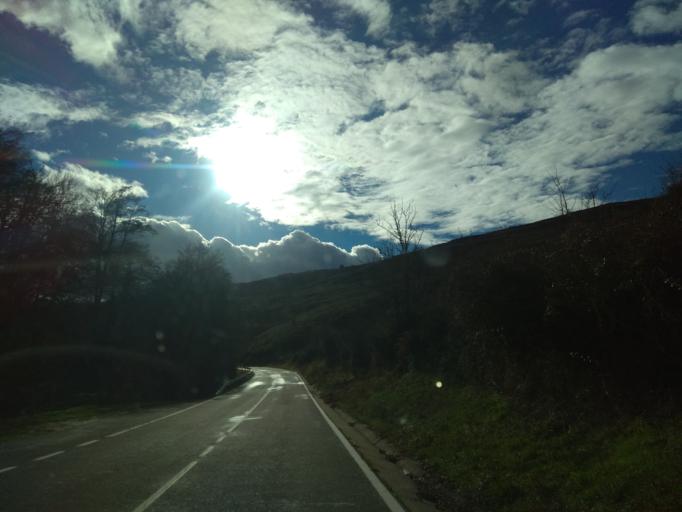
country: ES
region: Cantabria
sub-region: Provincia de Cantabria
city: San Martin de Elines
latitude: 42.8582
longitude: -3.9131
